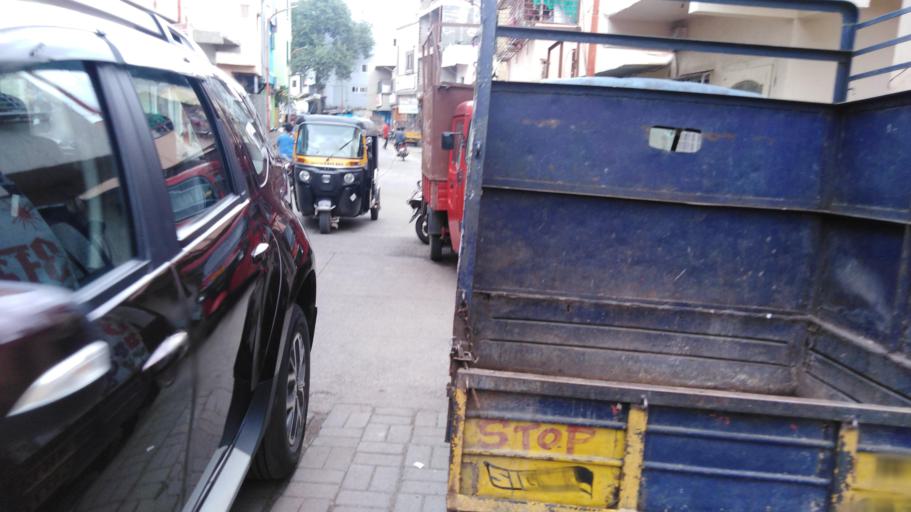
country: IN
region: Maharashtra
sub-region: Pune Division
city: Khadki
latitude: 18.5475
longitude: 73.8785
